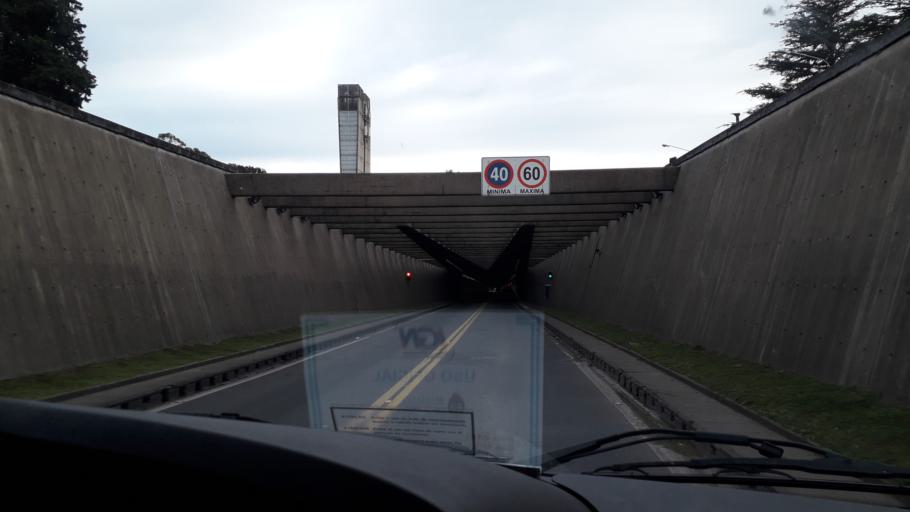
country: AR
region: Entre Rios
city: Parana
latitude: -31.7136
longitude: -60.5015
